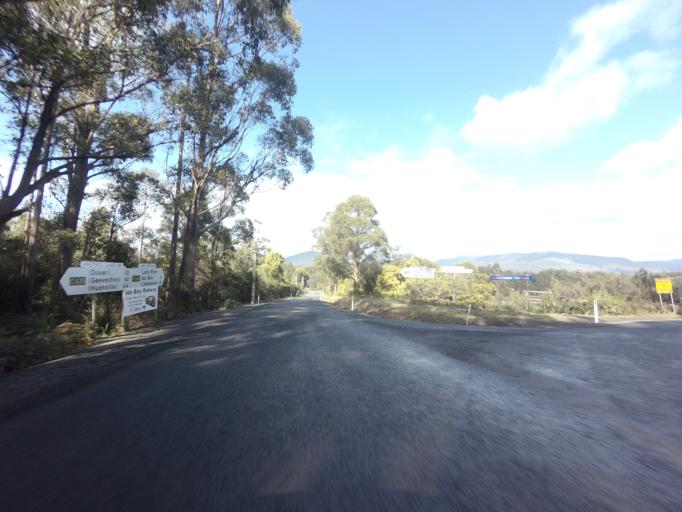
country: AU
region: Tasmania
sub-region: Huon Valley
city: Geeveston
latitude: -43.4119
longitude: 146.9073
